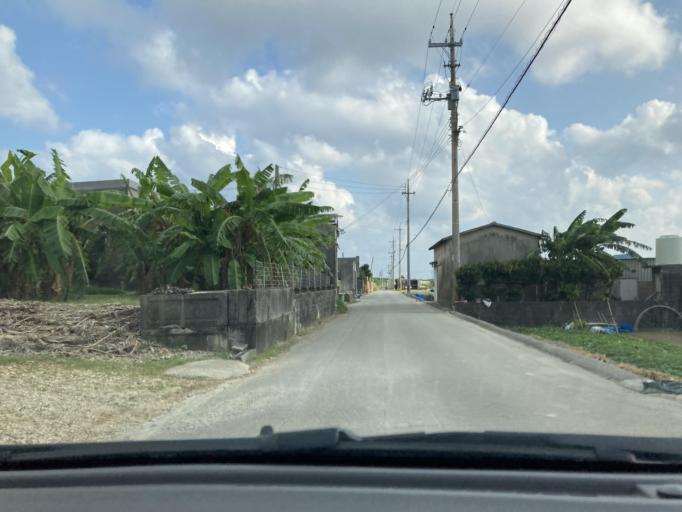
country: JP
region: Okinawa
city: Itoman
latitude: 26.0889
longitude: 127.6615
